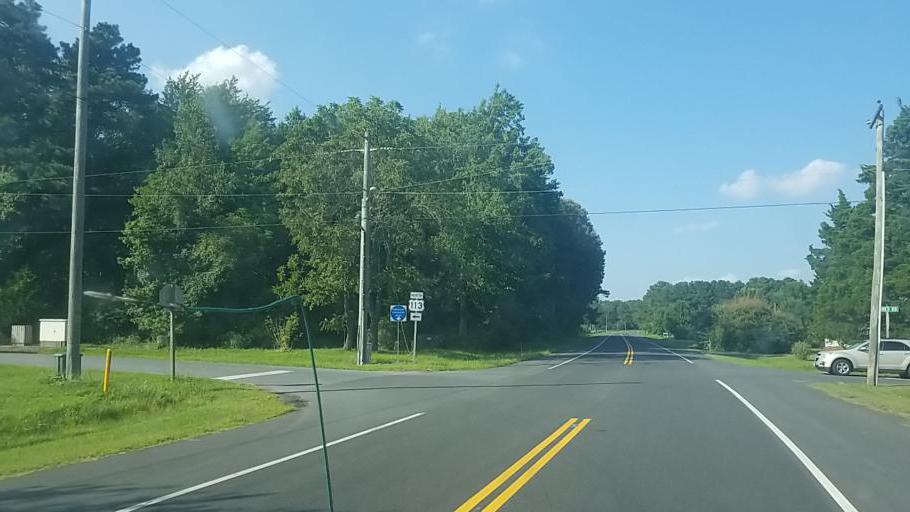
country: US
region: Maryland
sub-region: Worcester County
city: Berlin
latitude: 38.3653
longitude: -75.2013
